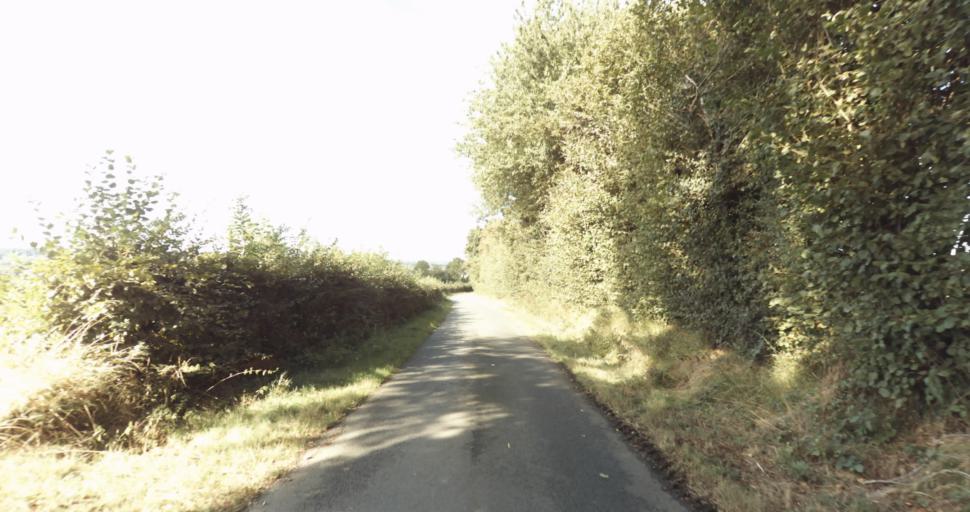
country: FR
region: Lower Normandy
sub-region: Departement de l'Orne
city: Vimoutiers
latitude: 48.9259
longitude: 0.1182
